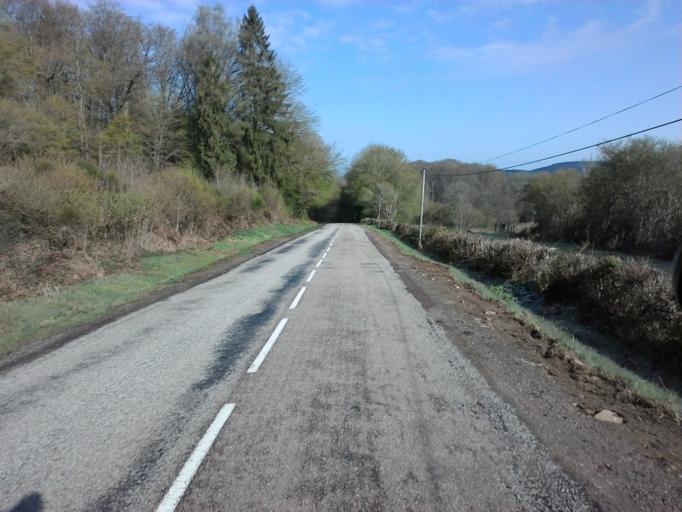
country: FR
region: Bourgogne
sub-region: Departement de la Cote-d'Or
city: Saulieu
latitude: 47.2469
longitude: 4.0690
